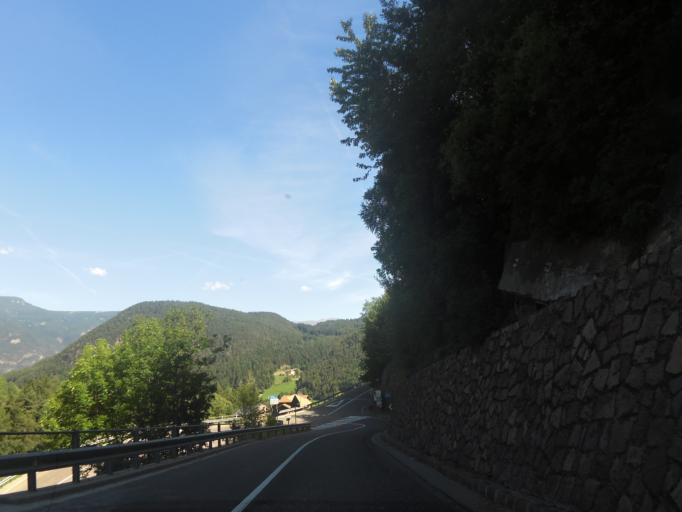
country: IT
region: Trentino-Alto Adige
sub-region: Bolzano
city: Castelrotto
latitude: 46.5643
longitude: 11.5544
